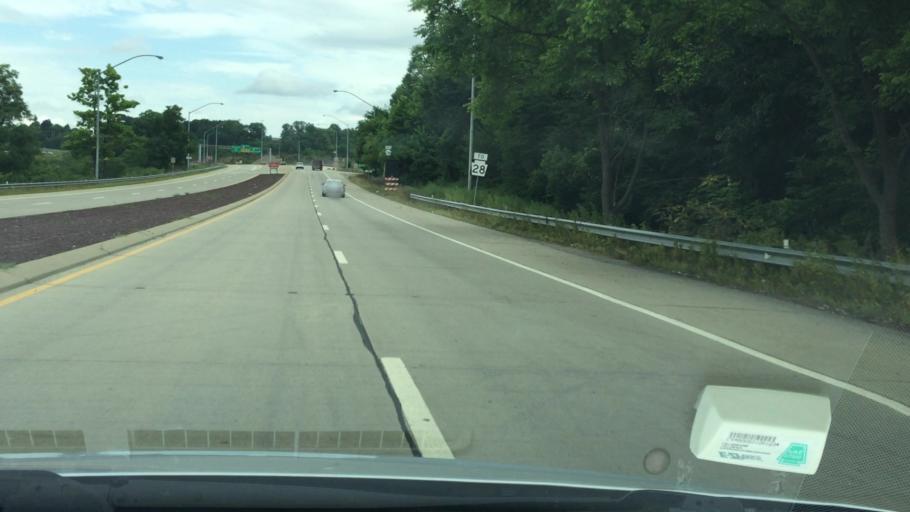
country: US
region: Pennsylvania
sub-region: Allegheny County
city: Tarentum
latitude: 40.6079
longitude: -79.7569
